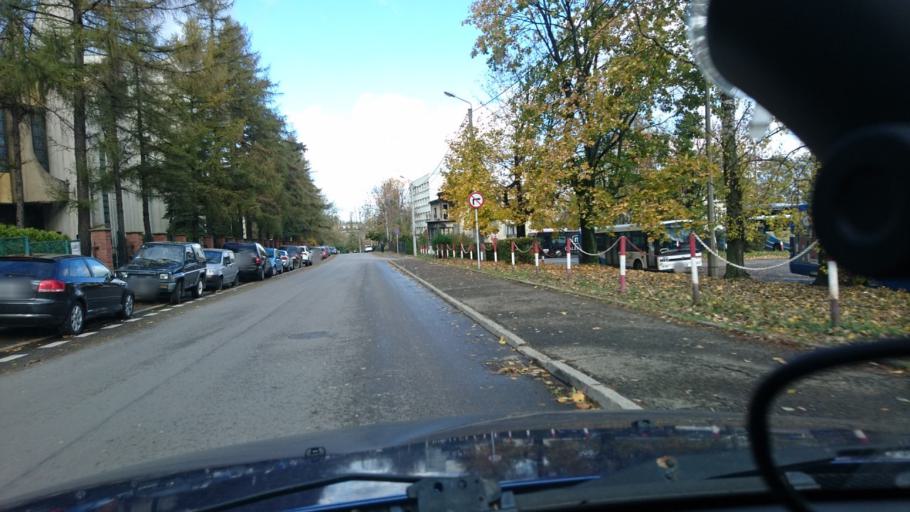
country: PL
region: Silesian Voivodeship
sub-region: Bielsko-Biala
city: Bielsko-Biala
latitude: 49.8302
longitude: 19.0419
